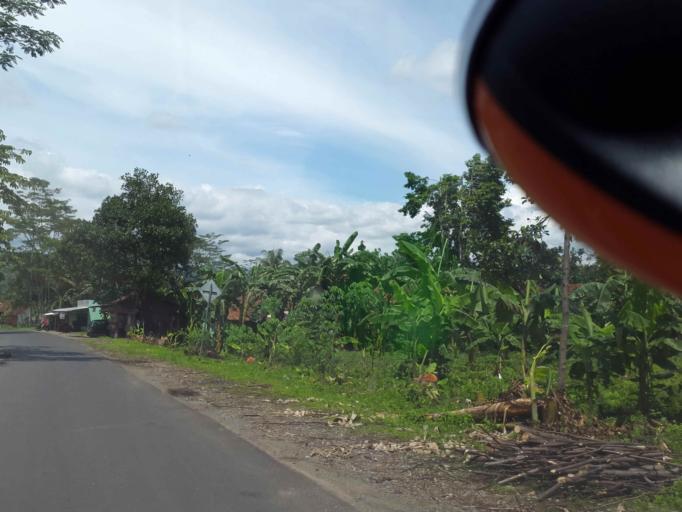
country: ID
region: Central Java
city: Purbalingga
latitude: -7.3902
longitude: 109.5951
